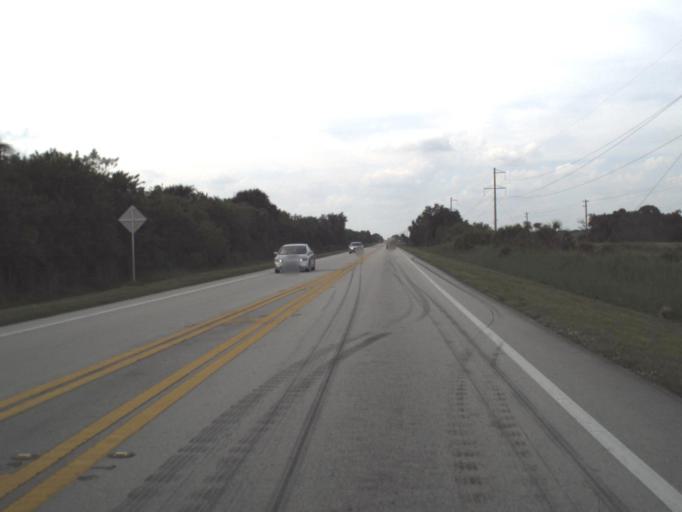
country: US
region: Florida
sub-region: Okeechobee County
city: Taylor Creek
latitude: 27.1631
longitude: -80.6833
